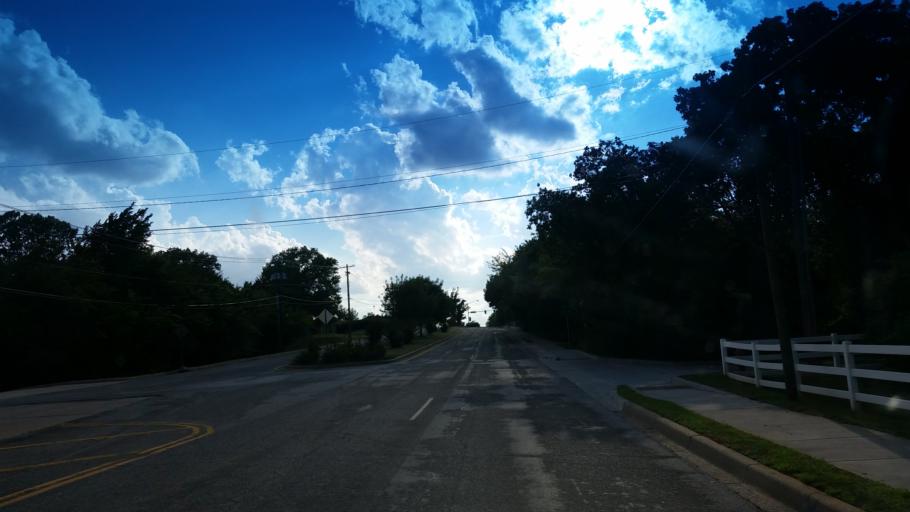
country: US
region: Oklahoma
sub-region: Oklahoma County
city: Nichols Hills
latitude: 35.5368
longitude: -97.4806
